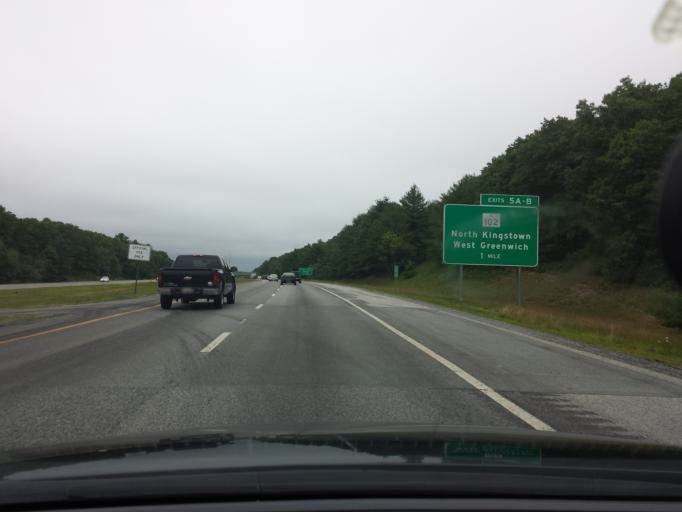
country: US
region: Rhode Island
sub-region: Kent County
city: West Greenwich
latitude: 41.5840
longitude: -71.6595
